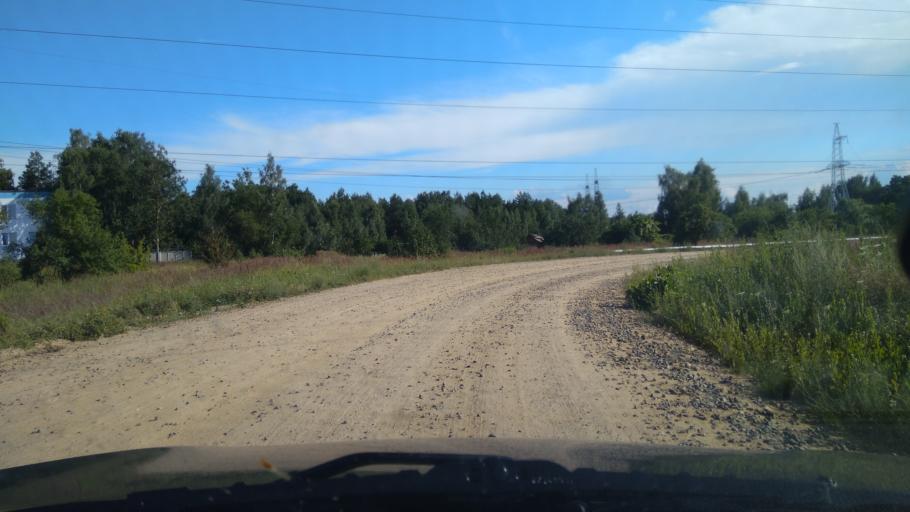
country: BY
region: Brest
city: Byelaazyorsk
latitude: 52.4546
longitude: 25.1874
